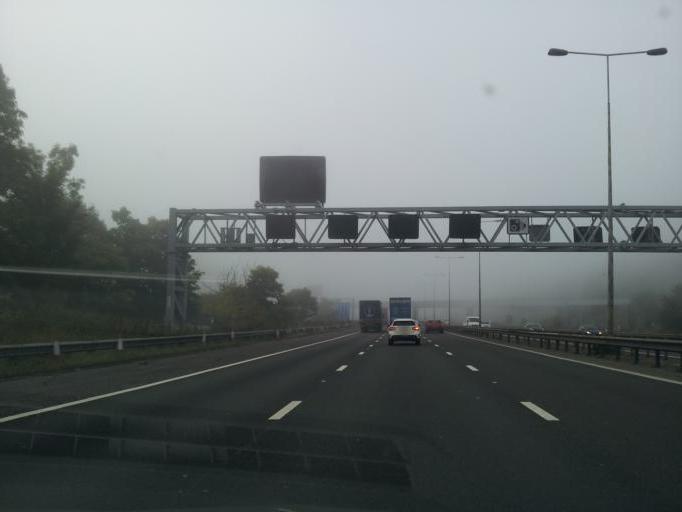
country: GB
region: England
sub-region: Kirklees
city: Cleckheaton
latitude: 53.7353
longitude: -1.7273
